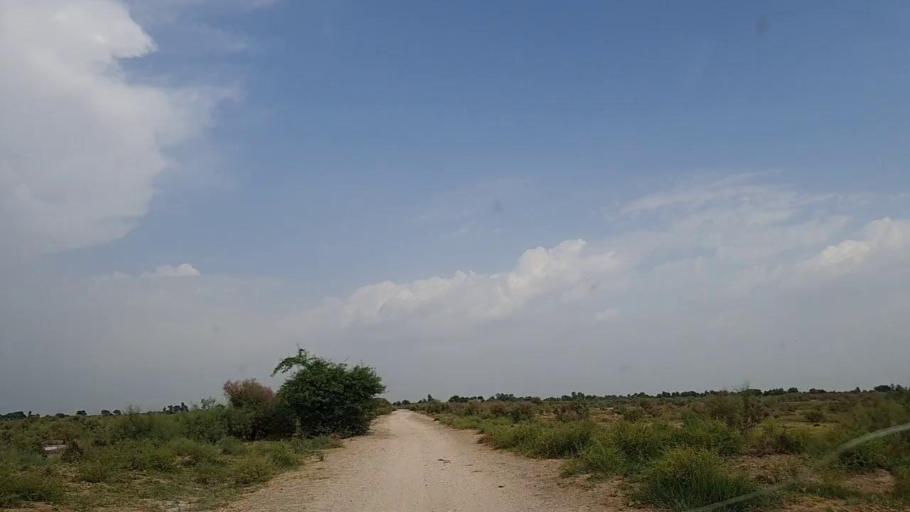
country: PK
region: Sindh
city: Khanpur
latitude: 27.8200
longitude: 69.5282
